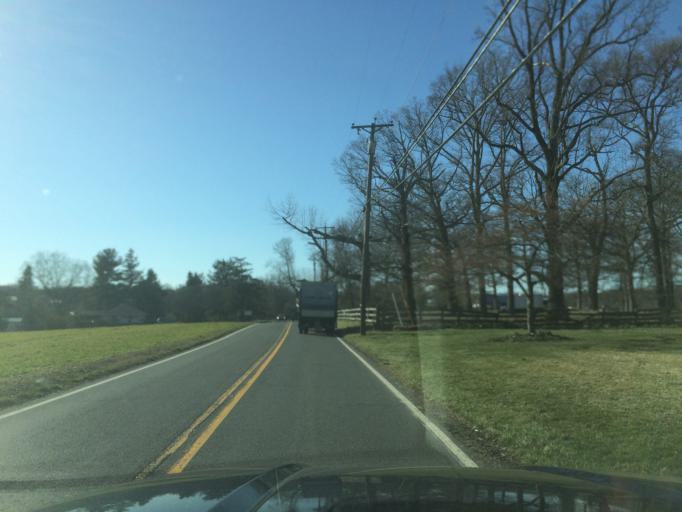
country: US
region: Maryland
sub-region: Montgomery County
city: Olney
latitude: 39.2240
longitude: -77.0626
